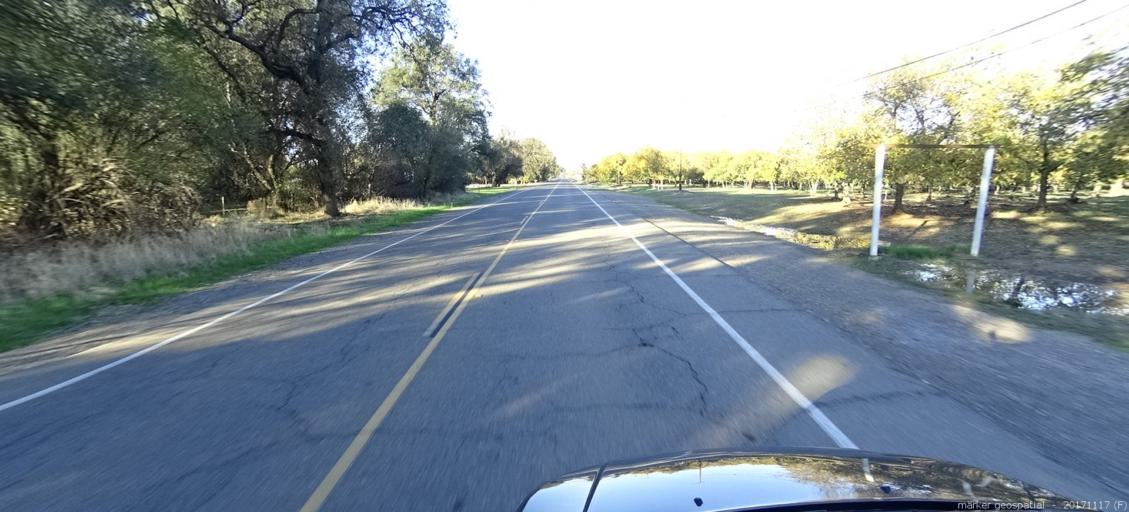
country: US
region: California
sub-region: Shasta County
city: Anderson
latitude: 40.4675
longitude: -122.2431
